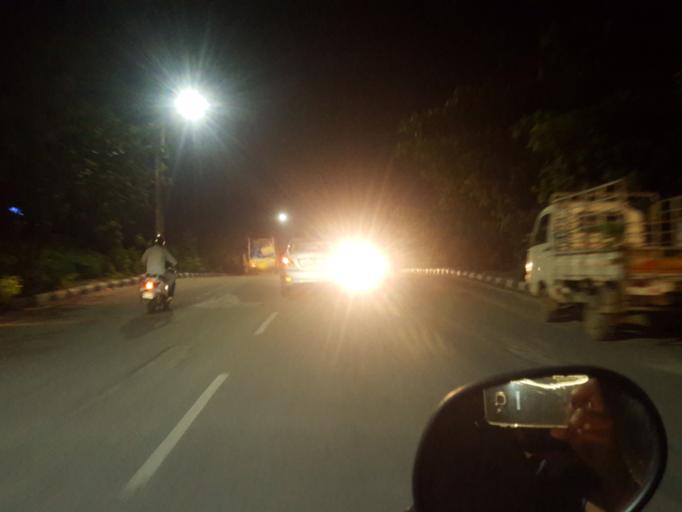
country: IN
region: Telangana
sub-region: Rangareddi
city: Kukatpalli
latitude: 17.4406
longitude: 78.3717
